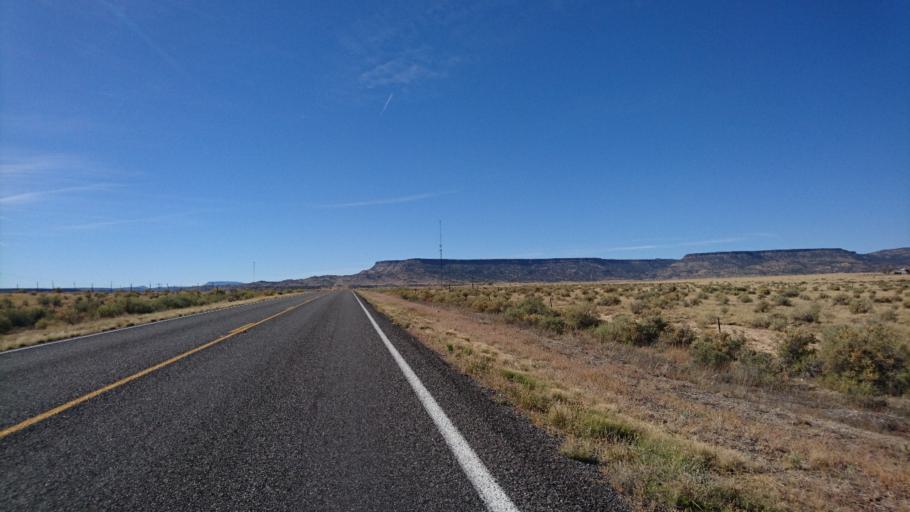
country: US
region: New Mexico
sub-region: Cibola County
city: Skyline-Ganipa
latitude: 35.0824
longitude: -107.6244
